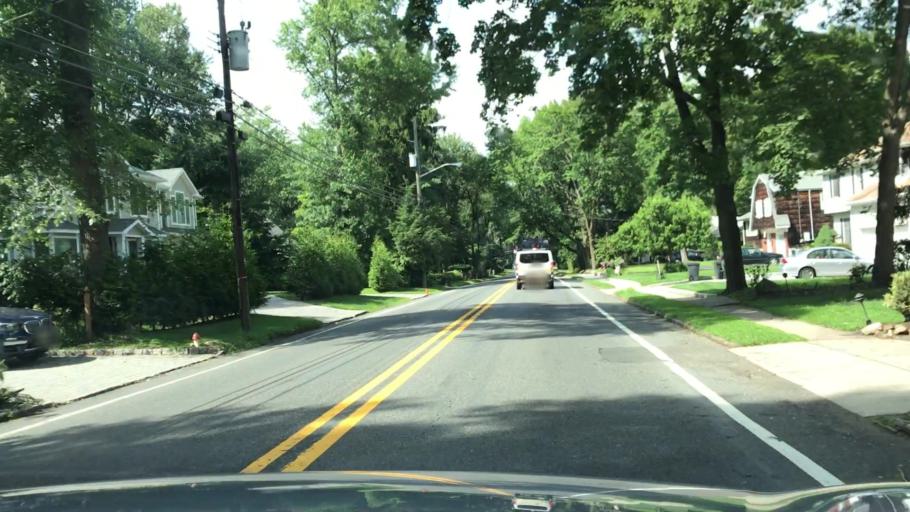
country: US
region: New Jersey
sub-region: Bergen County
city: Demarest
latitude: 40.9555
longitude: -73.9754
